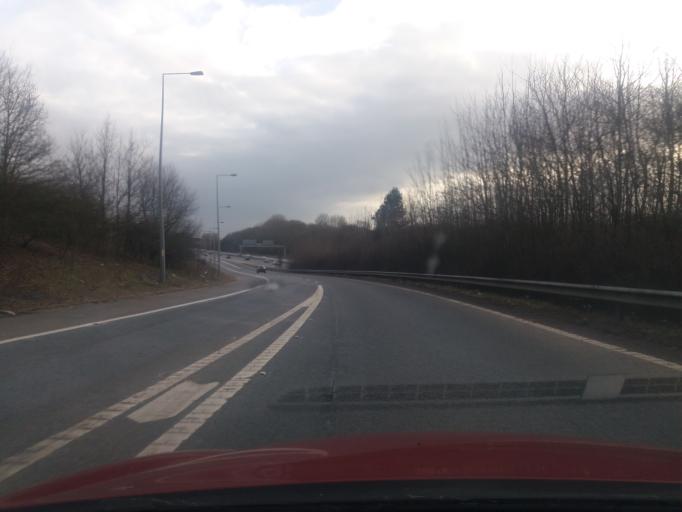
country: GB
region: England
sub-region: Lancashire
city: Clayton-le-Woods
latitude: 53.7168
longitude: -2.6291
